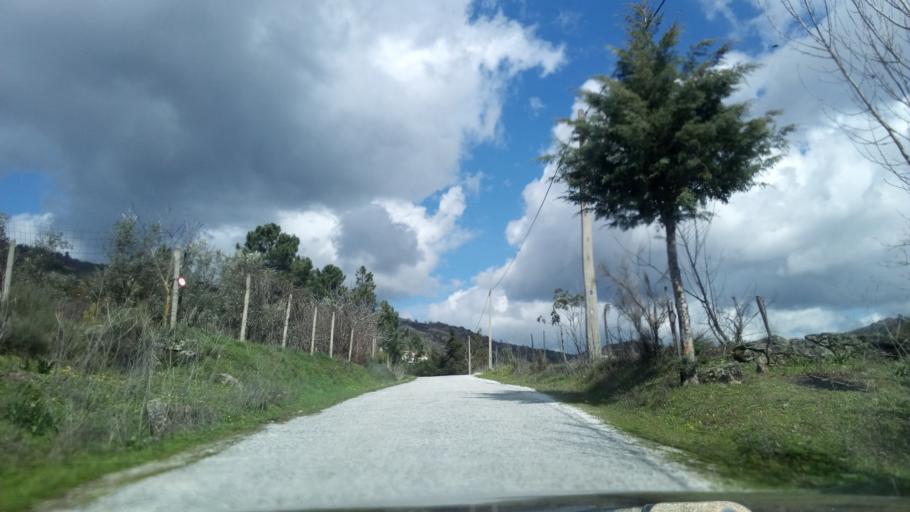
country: PT
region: Guarda
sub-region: Fornos de Algodres
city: Fornos de Algodres
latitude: 40.6558
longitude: -7.4979
